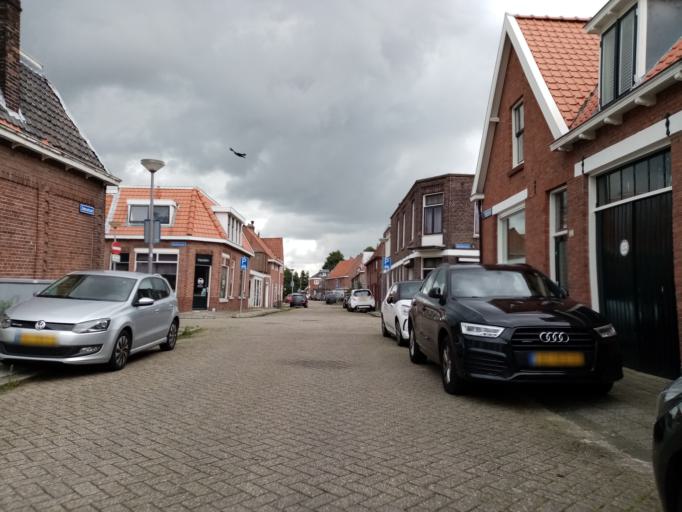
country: NL
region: South Holland
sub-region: Gemeente Rotterdam
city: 's-Gravenland
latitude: 51.9121
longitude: 4.5524
